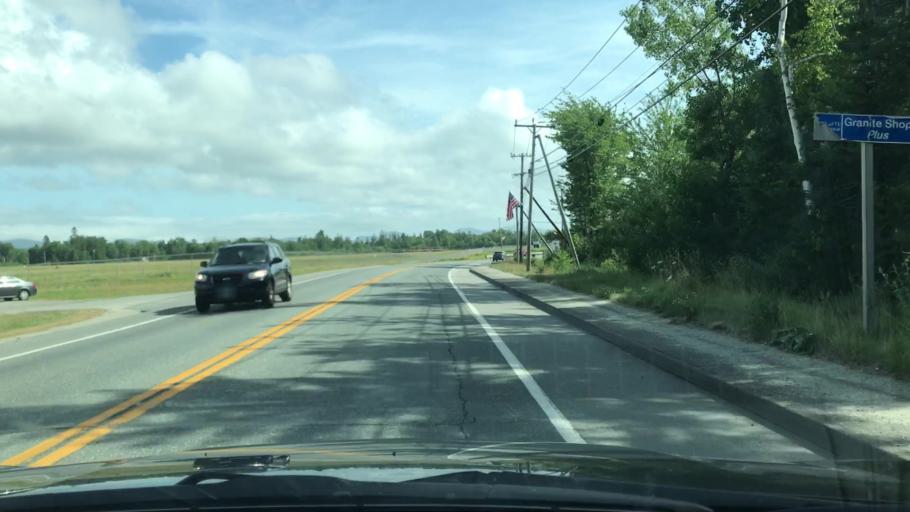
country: US
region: Maine
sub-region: Hancock County
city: Trenton
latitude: 44.4463
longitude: -68.3695
